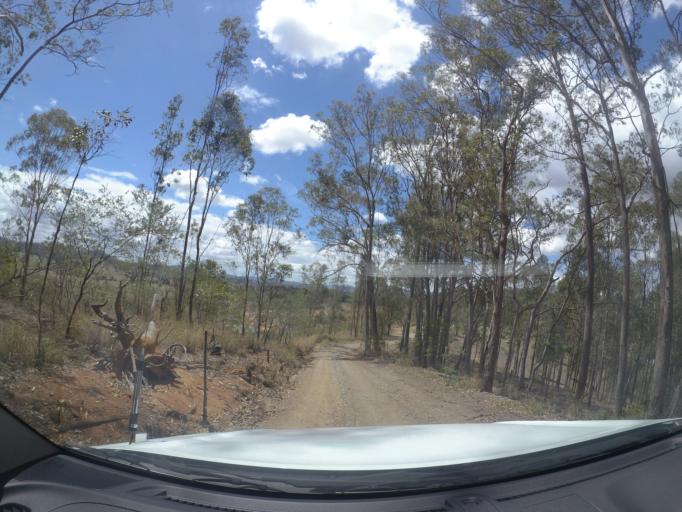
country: AU
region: Queensland
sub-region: Logan
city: Cedar Vale
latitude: -27.9162
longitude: 153.0487
